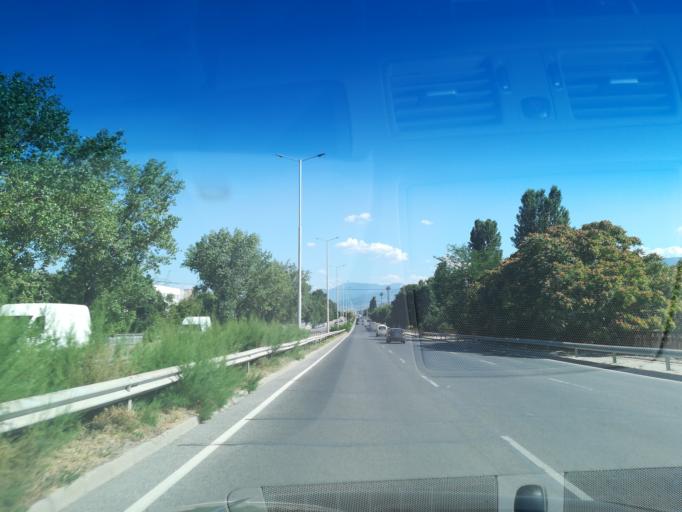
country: BG
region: Plovdiv
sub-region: Obshtina Plovdiv
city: Plovdiv
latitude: 42.1146
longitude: 24.7780
